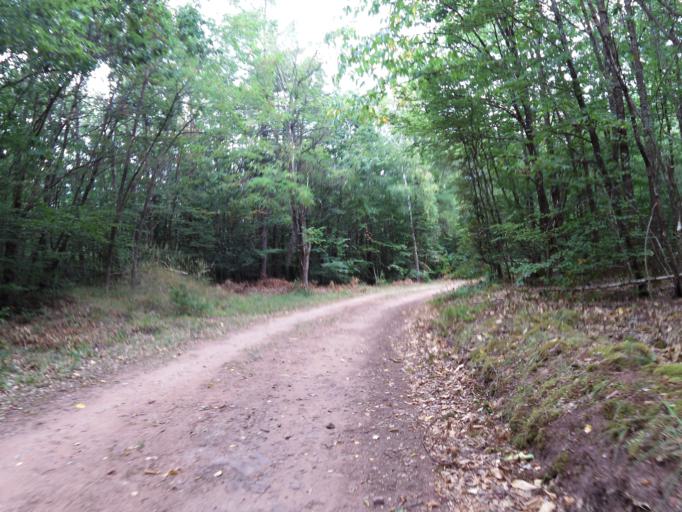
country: DE
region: Rheinland-Pfalz
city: Elmstein
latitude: 49.3855
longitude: 7.9438
